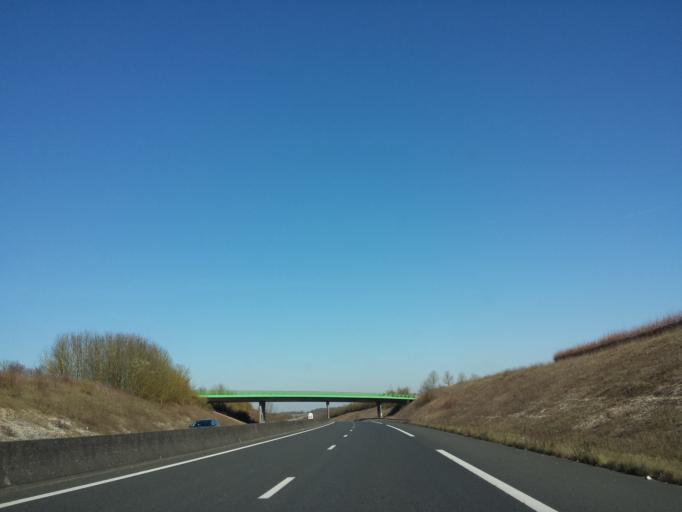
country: FR
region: Picardie
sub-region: Departement de l'Oise
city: Tille
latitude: 49.5211
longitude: 2.1865
